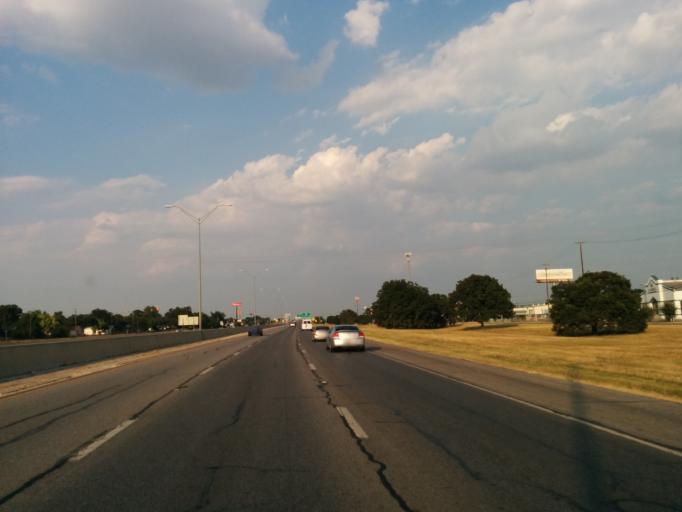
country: US
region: Texas
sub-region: Bexar County
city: Kirby
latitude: 29.4293
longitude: -98.4141
